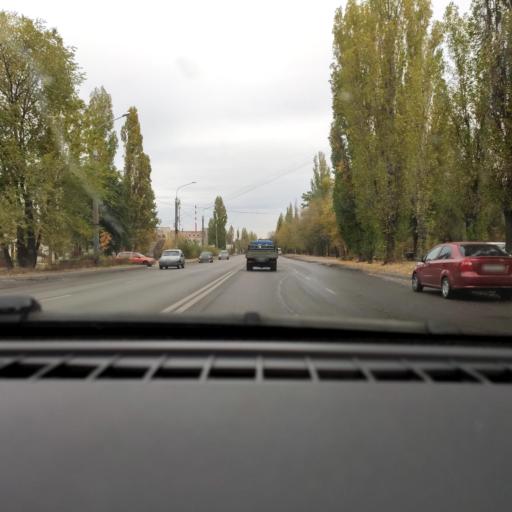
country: RU
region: Voronezj
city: Maslovka
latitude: 51.6349
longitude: 39.2636
